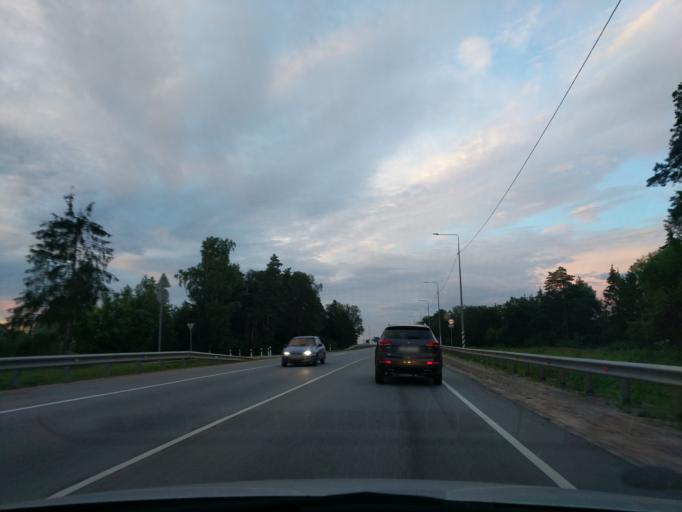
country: RU
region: Kaluga
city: Obninsk
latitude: 55.0477
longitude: 36.5558
